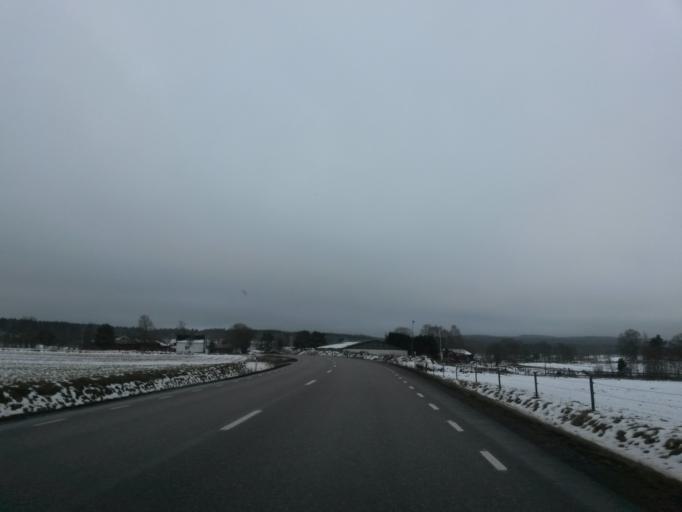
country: SE
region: Vaestra Goetaland
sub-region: Vargarda Kommun
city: Vargarda
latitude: 58.0003
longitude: 12.8112
